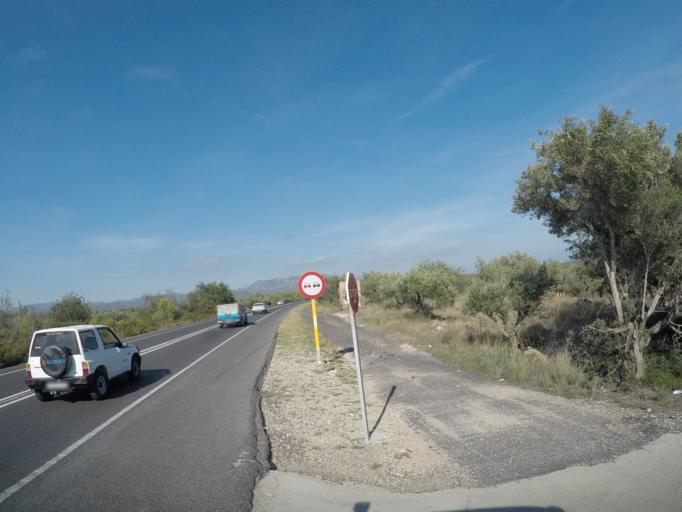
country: ES
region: Catalonia
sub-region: Provincia de Tarragona
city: El Perello
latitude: 40.8952
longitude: 0.7290
